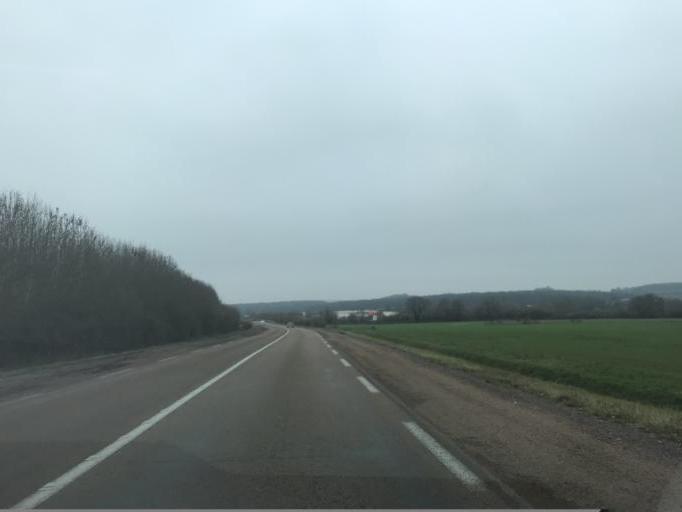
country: FR
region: Bourgogne
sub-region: Departement de l'Yonne
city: Avallon
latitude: 47.4963
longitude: 3.9345
